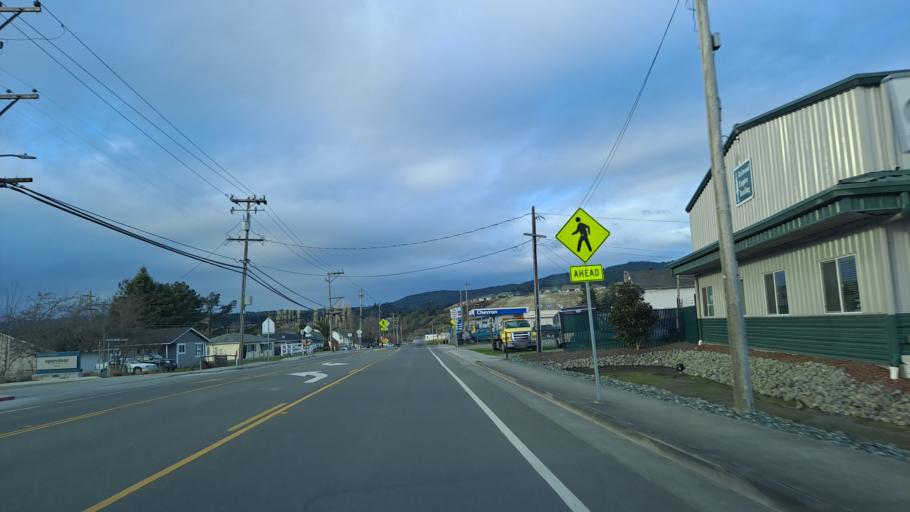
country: US
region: California
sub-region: Humboldt County
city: Fortuna
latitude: 40.5818
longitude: -124.1307
